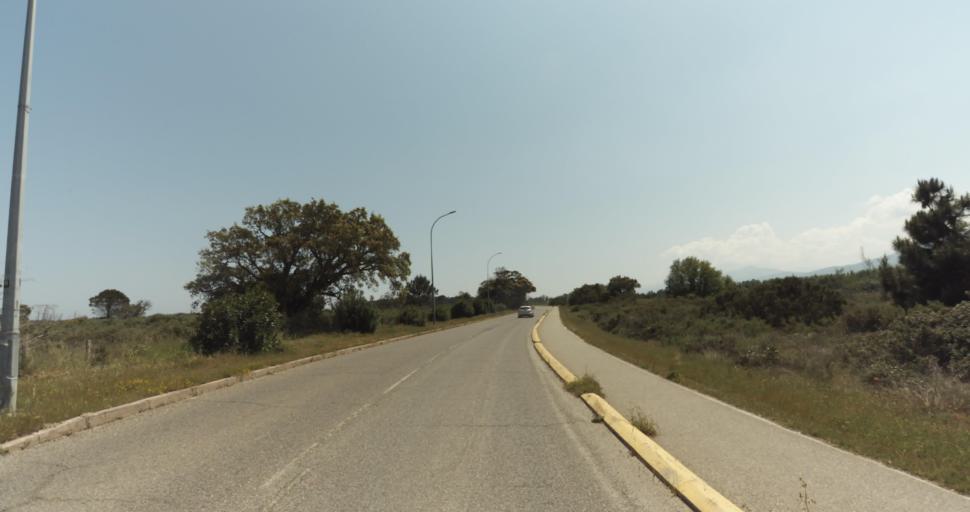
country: FR
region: Corsica
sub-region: Departement de la Haute-Corse
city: Biguglia
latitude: 42.6543
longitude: 9.4500
